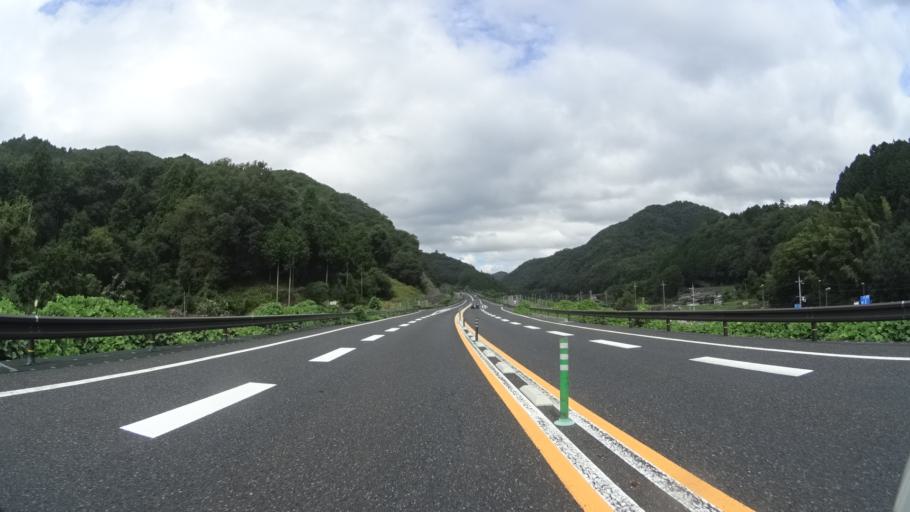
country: JP
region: Hyogo
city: Yamazakicho-nakabirose
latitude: 35.0575
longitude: 134.3659
